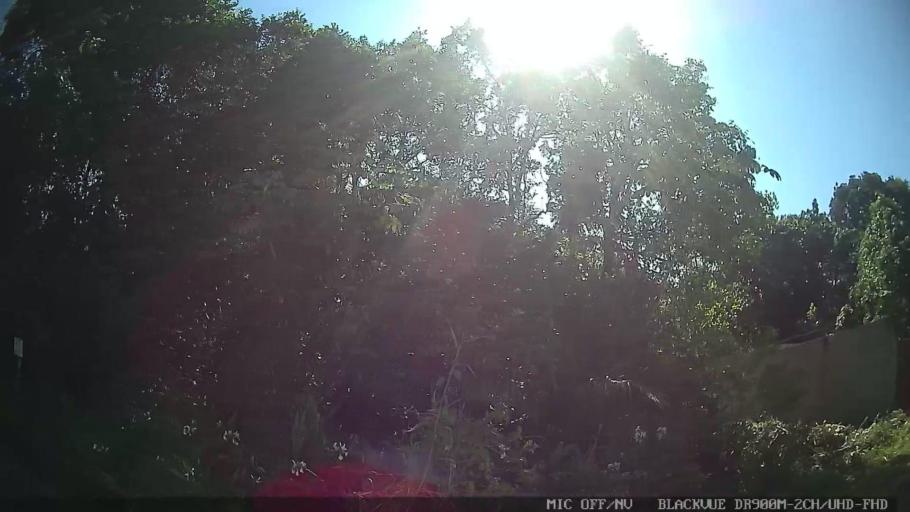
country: BR
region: Sao Paulo
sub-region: Itanhaem
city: Itanhaem
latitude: -24.1464
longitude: -46.7386
